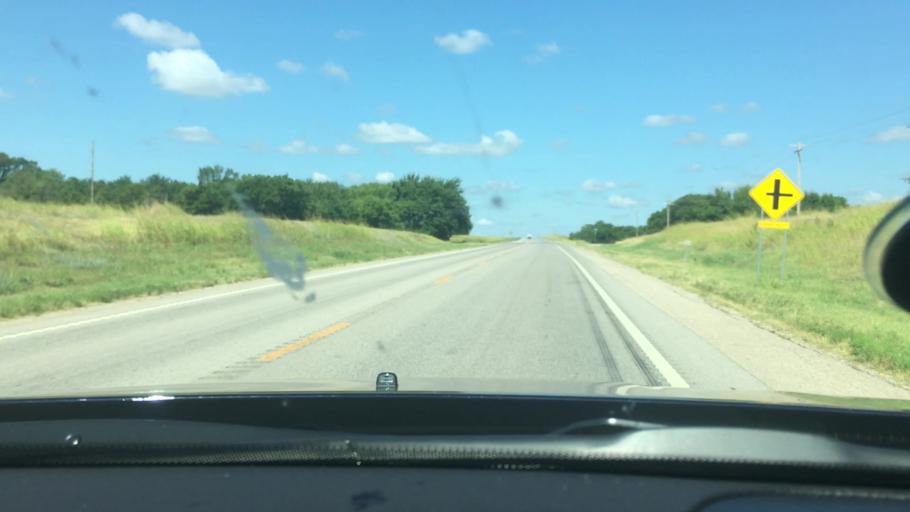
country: US
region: Oklahoma
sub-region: Marshall County
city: Oakland
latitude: 34.1002
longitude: -96.8265
